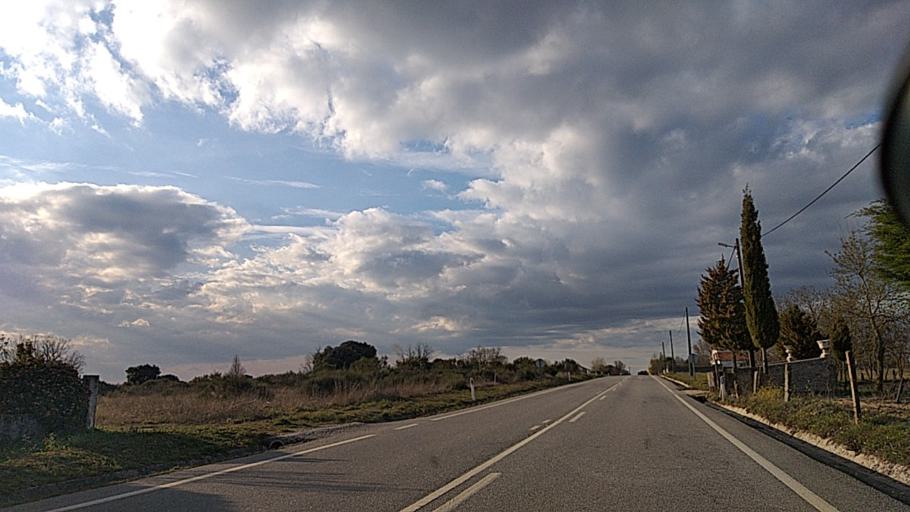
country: ES
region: Castille and Leon
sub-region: Provincia de Salamanca
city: Aldea del Obispo
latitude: 40.7023
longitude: -6.8927
